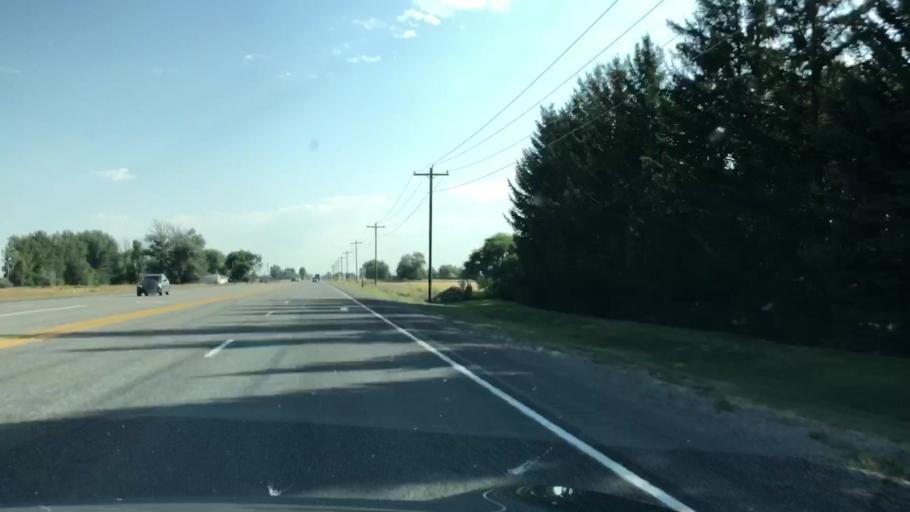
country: US
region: Idaho
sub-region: Bonneville County
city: Iona
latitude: 43.5654
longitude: -111.9238
